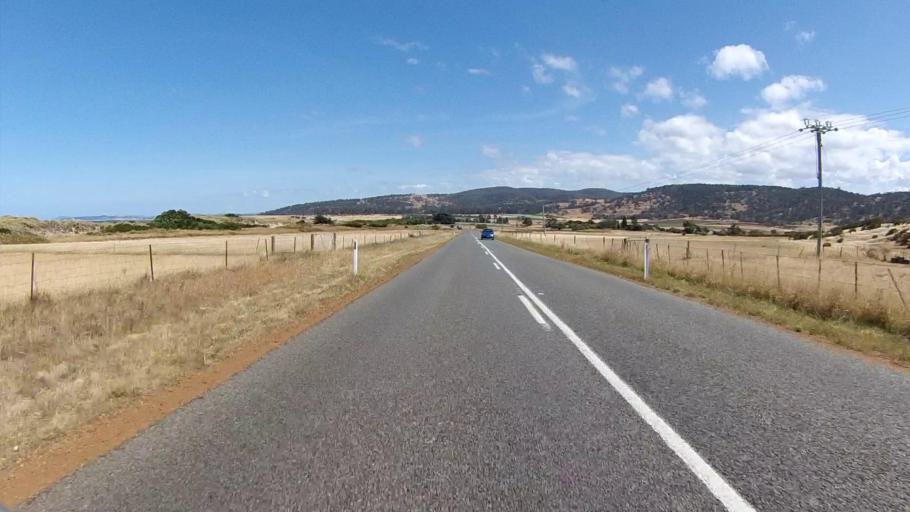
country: AU
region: Tasmania
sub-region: Sorell
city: Sorell
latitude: -42.1957
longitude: 148.0536
